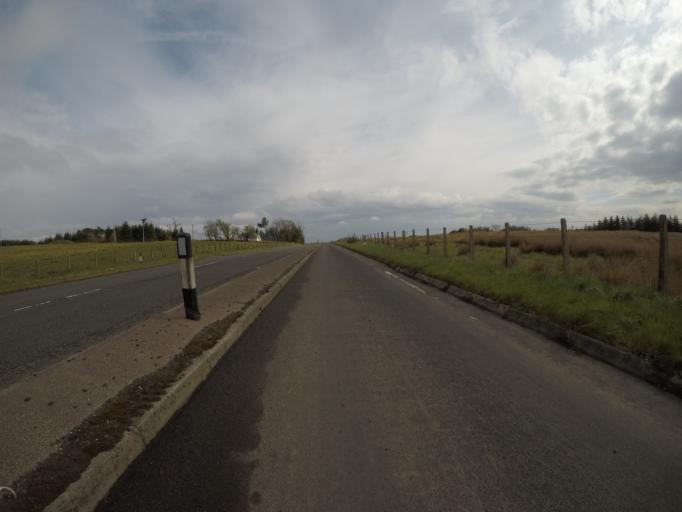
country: GB
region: Scotland
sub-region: East Renfrewshire
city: Neilston
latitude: 55.7073
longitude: -4.3986
